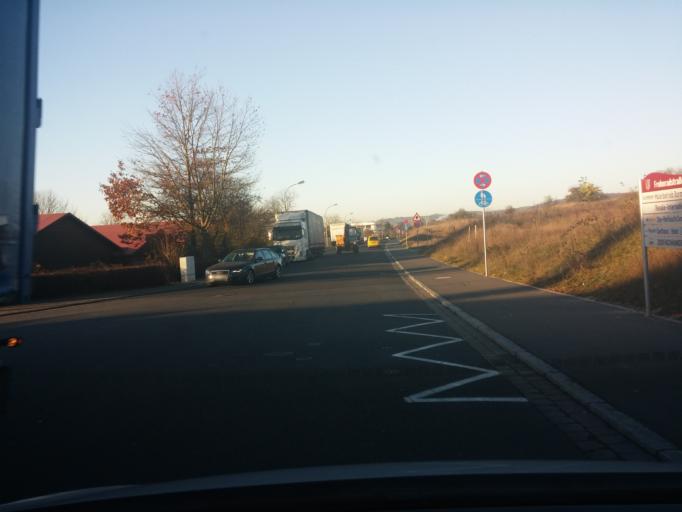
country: DE
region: Bavaria
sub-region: Regierungsbezirk Unterfranken
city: Hosbach
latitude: 50.0103
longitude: 9.2214
